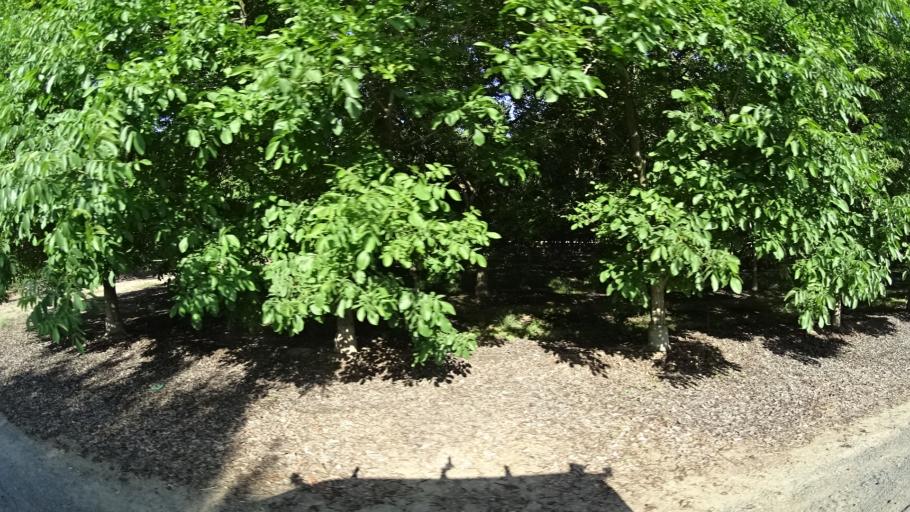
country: US
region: California
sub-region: Kings County
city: Home Garden
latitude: 36.2865
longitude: -119.5652
